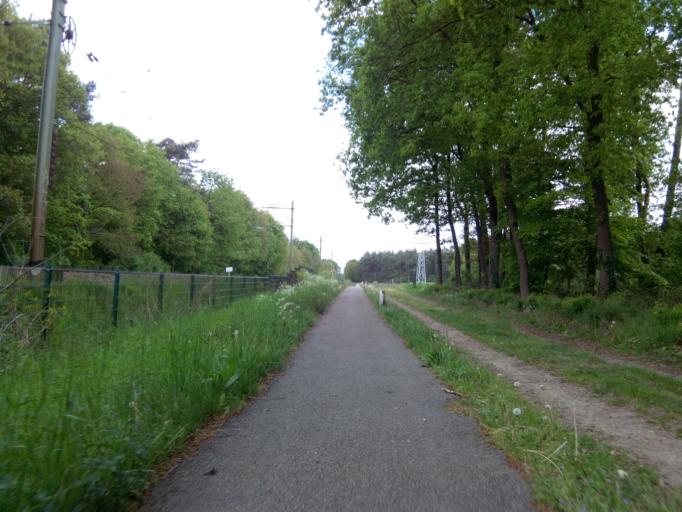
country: NL
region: Gelderland
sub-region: Gemeente Ede
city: Ede
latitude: 52.0550
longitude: 5.6628
